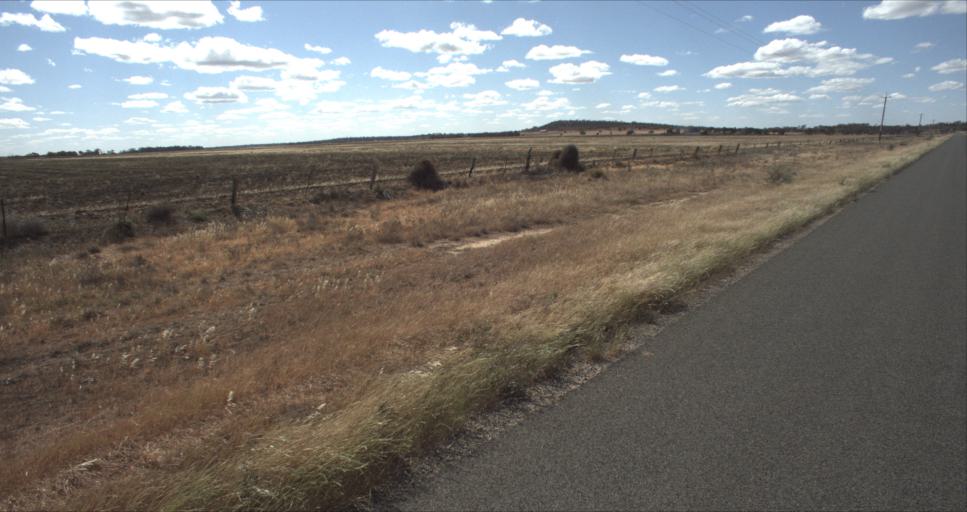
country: AU
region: New South Wales
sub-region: Leeton
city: Leeton
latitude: -34.4385
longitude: 146.2568
